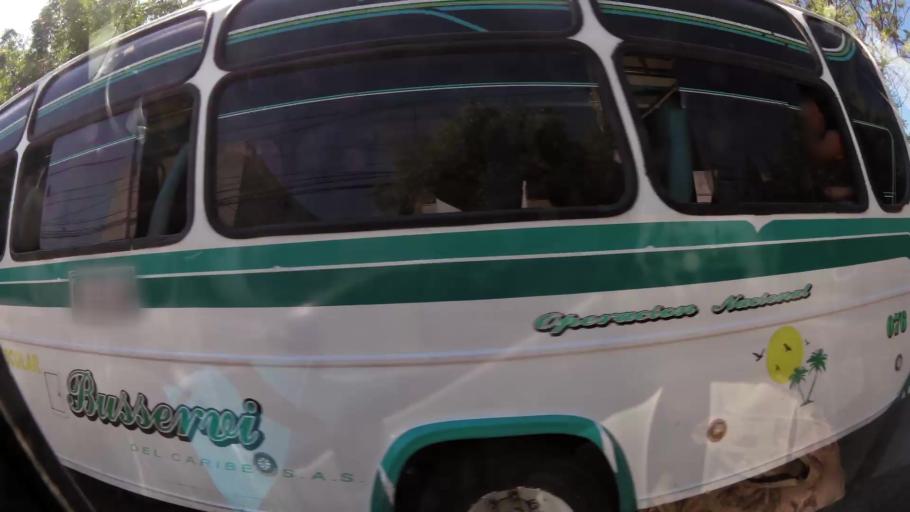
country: CO
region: Atlantico
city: Barranquilla
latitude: 10.9724
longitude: -74.7883
